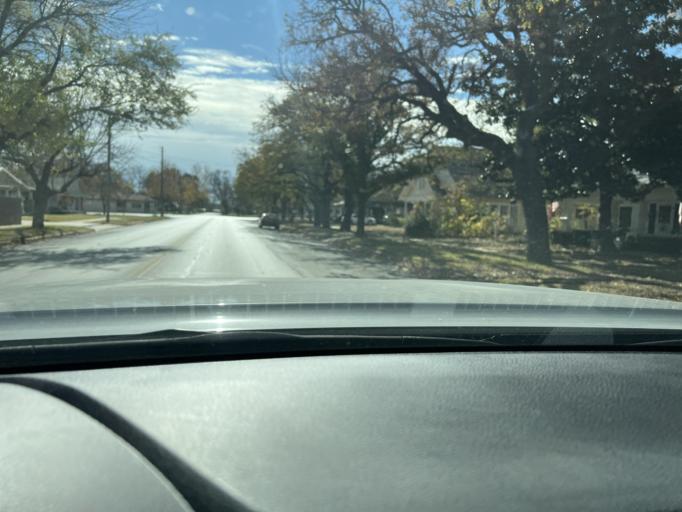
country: US
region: Texas
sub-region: Eastland County
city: Eastland
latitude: 32.3901
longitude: -98.8181
